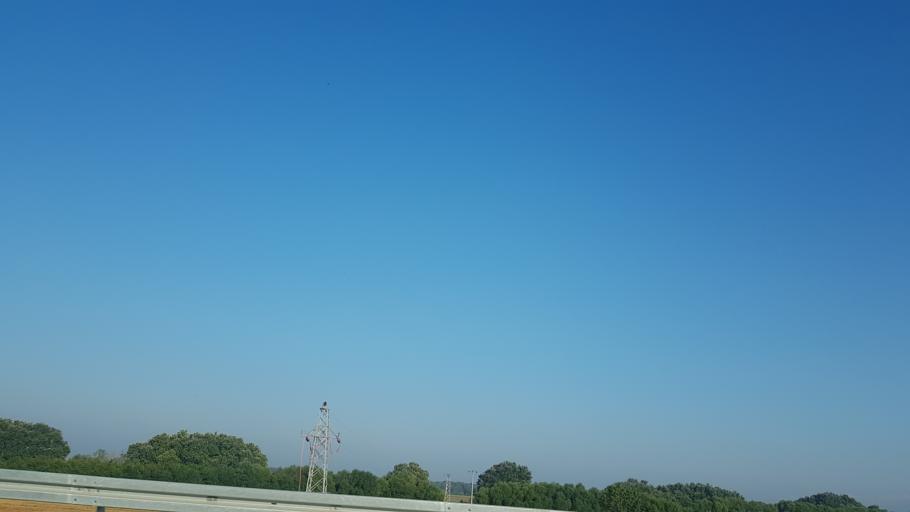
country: TR
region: Bursa
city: Karacabey
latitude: 40.1553
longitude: 28.3118
